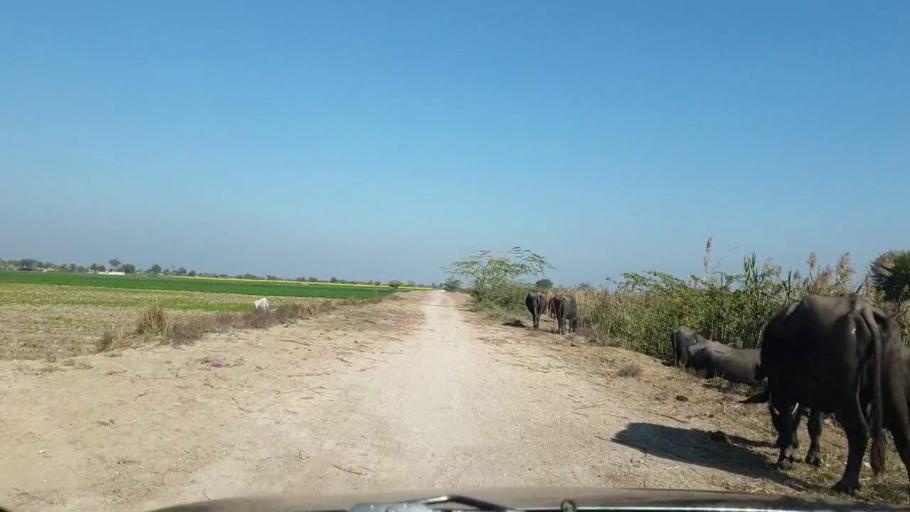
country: PK
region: Sindh
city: Sinjhoro
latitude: 25.9662
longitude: 68.7522
